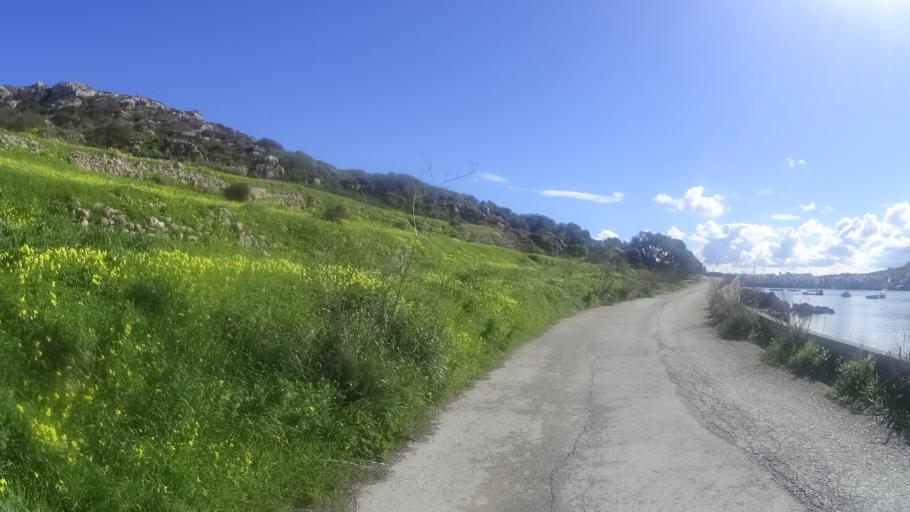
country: MT
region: Saint Paul's Bay
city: San Pawl il-Bahar
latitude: 35.9595
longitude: 14.3918
